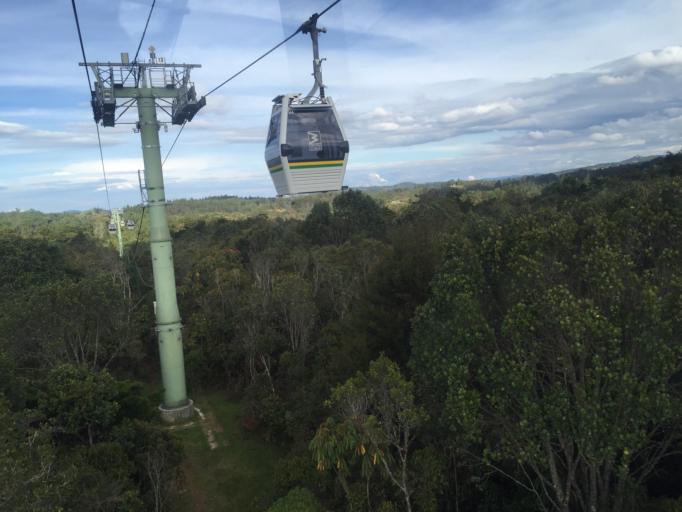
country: CO
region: Antioquia
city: Medellin
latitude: 6.2877
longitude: -75.5242
